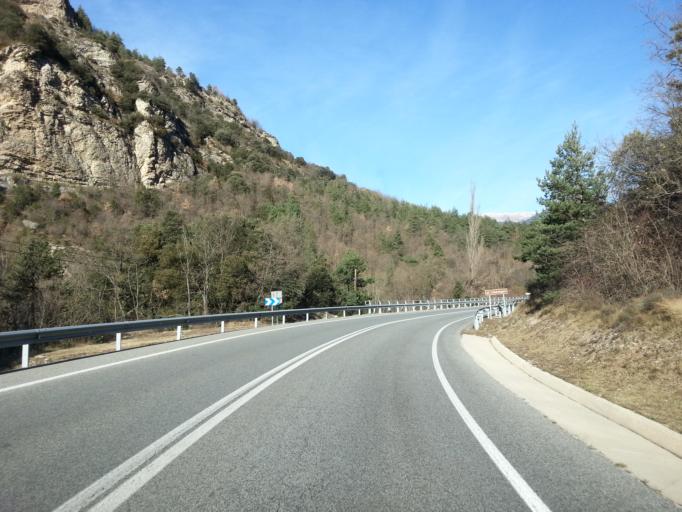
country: ES
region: Catalonia
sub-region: Provincia de Barcelona
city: Guardiola de Bergueda
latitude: 42.2108
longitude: 1.8684
